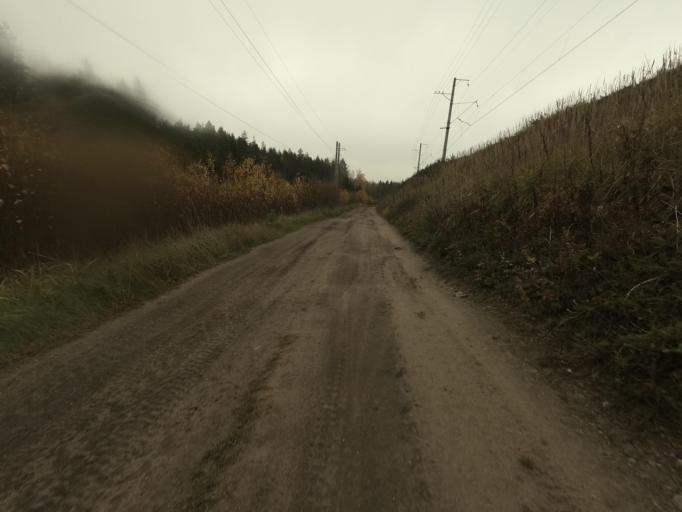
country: RU
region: Leningrad
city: Pavlovo
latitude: 59.7688
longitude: 30.9179
